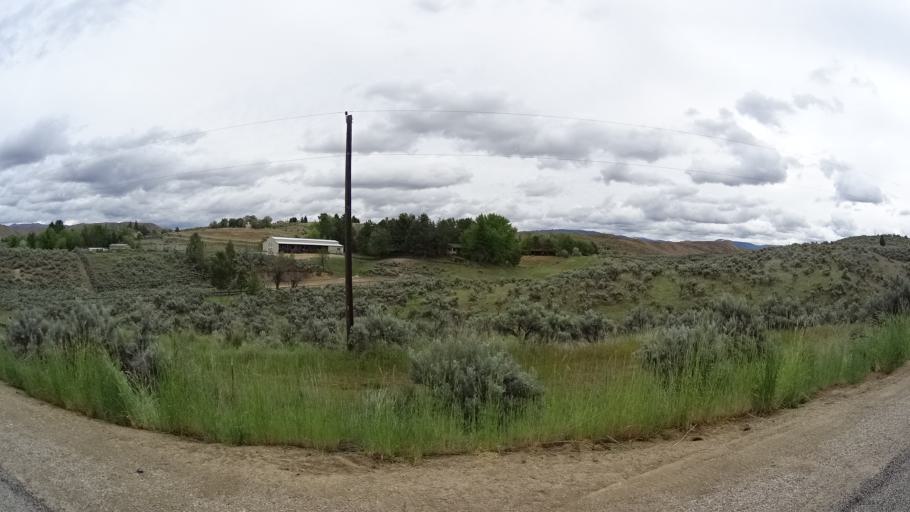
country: US
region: Idaho
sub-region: Ada County
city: Eagle
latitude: 43.7167
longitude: -116.3181
